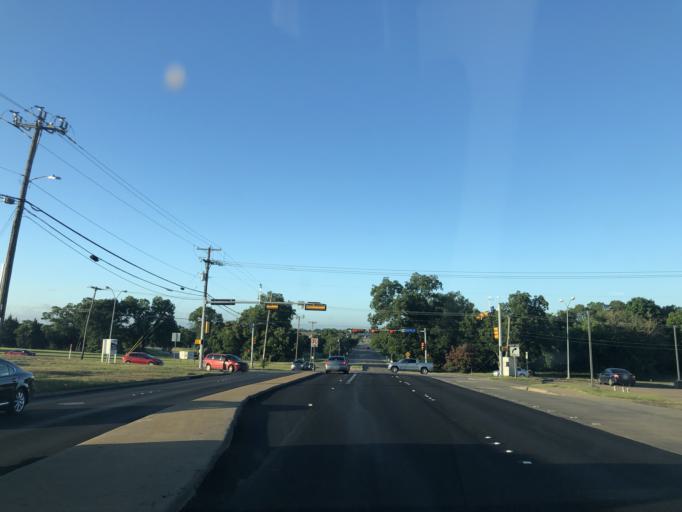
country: US
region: Texas
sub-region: Dallas County
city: Duncanville
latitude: 32.6345
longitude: -96.9084
